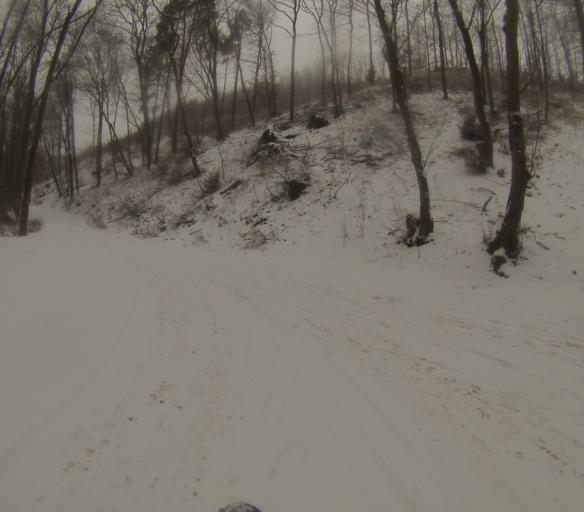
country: CZ
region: South Moravian
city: Orechov
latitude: 49.1360
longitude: 16.5266
